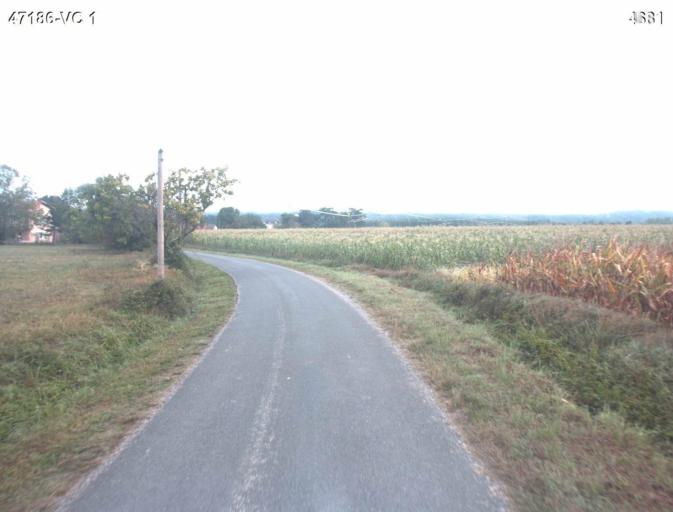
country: FR
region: Aquitaine
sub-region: Departement du Lot-et-Garonne
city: Port-Sainte-Marie
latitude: 44.2263
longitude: 0.4385
